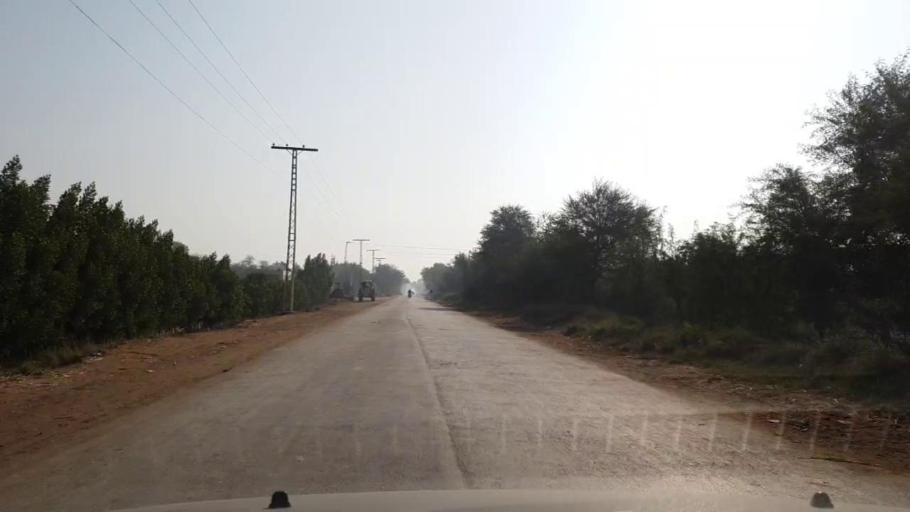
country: PK
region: Sindh
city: Matiari
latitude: 25.6005
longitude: 68.4531
